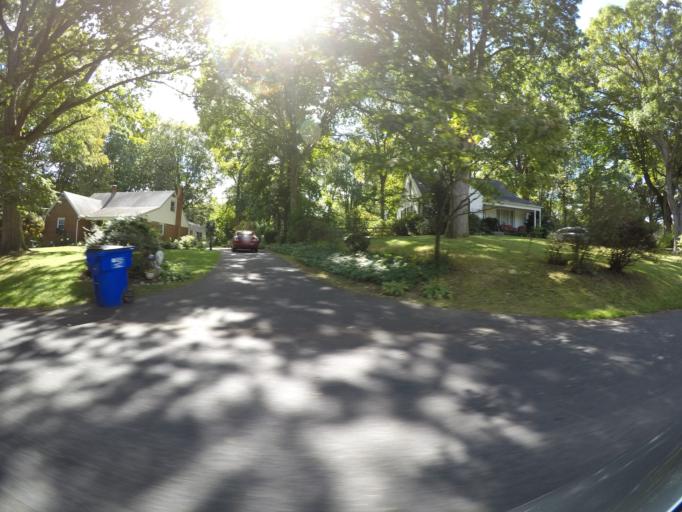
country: US
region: Maryland
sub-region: Harford County
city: South Bel Air
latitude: 39.5276
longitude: -76.3329
